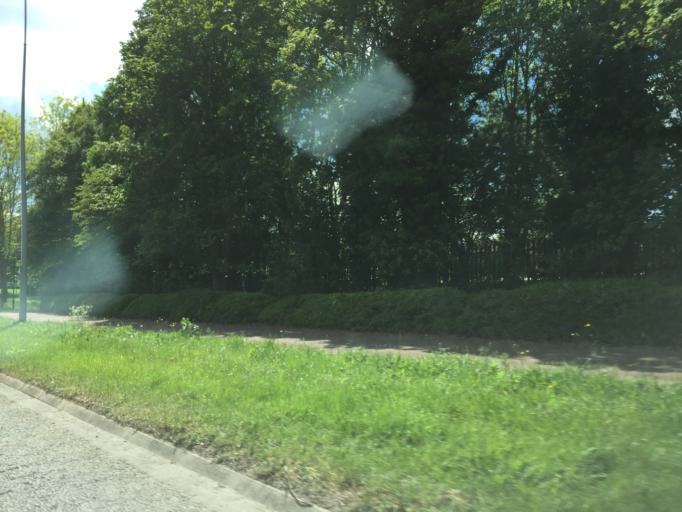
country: GB
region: England
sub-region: Milton Keynes
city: Simpson
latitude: 52.0211
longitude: -0.7258
